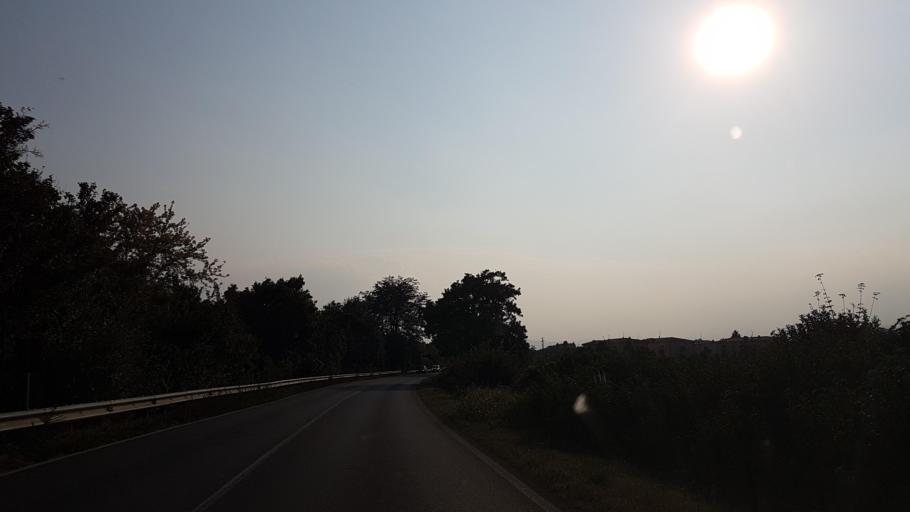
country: IT
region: Emilia-Romagna
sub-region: Provincia di Parma
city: Gaiano
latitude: 44.7268
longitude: 10.1791
